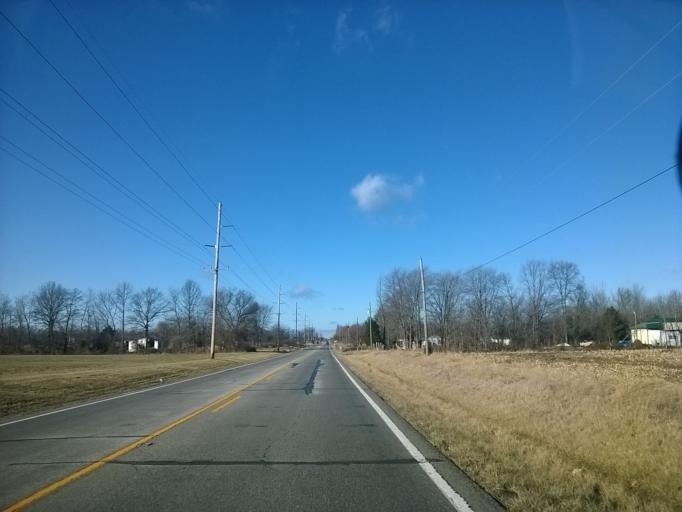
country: US
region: Indiana
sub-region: Scott County
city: Scottsburg
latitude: 38.7368
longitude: -85.6731
